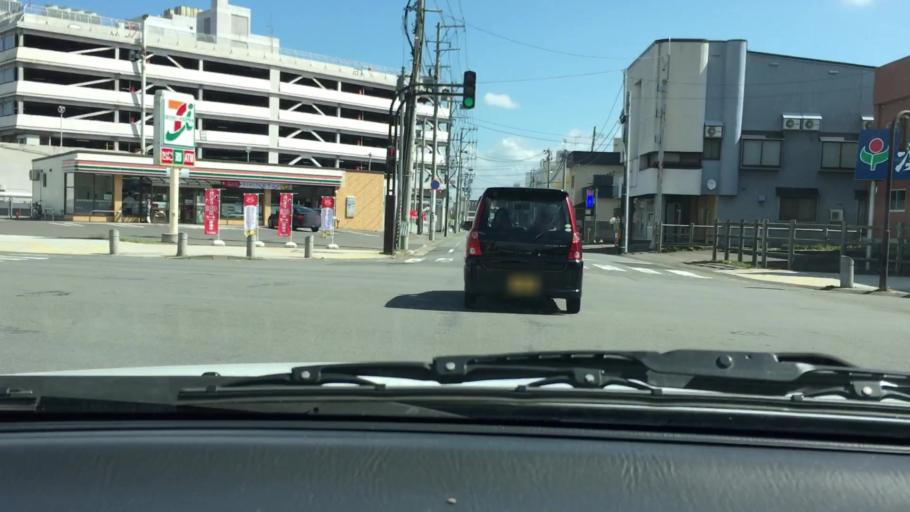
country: JP
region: Aomori
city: Hirosaki
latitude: 40.5984
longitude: 140.4801
